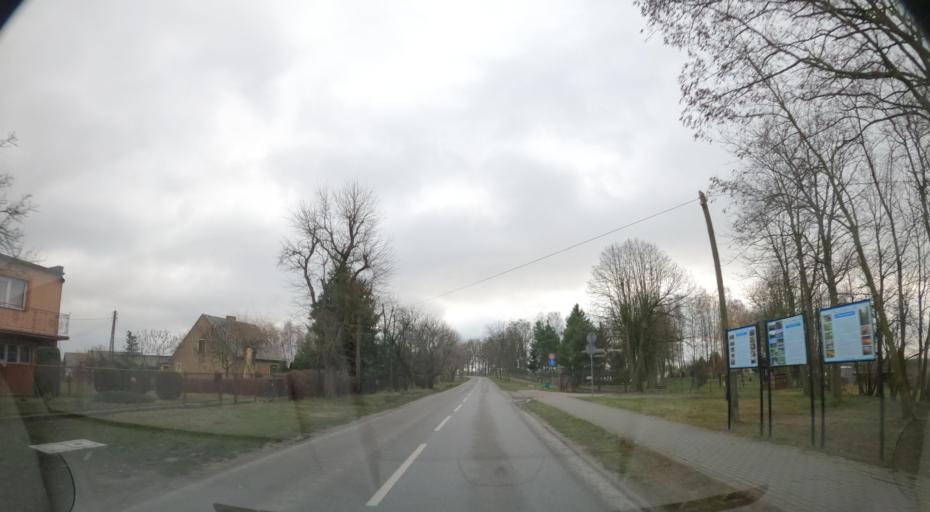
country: PL
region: Greater Poland Voivodeship
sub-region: Powiat pilski
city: Lobzenica
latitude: 53.2573
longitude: 17.2626
